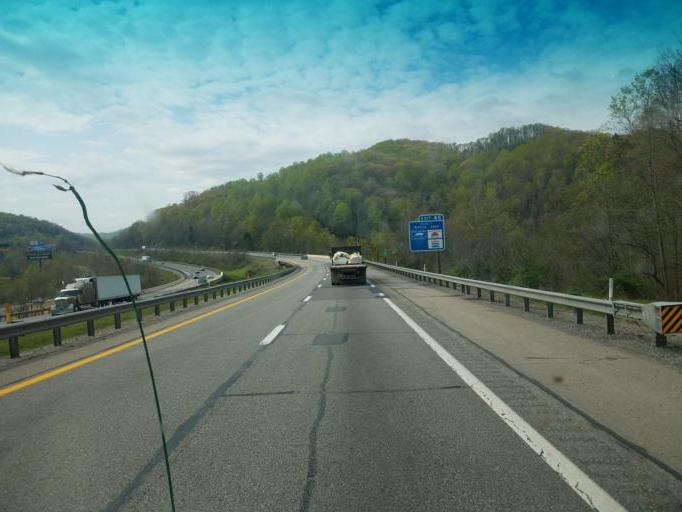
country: US
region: West Virginia
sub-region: Raleigh County
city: Bradley
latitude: 37.8811
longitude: -81.2674
